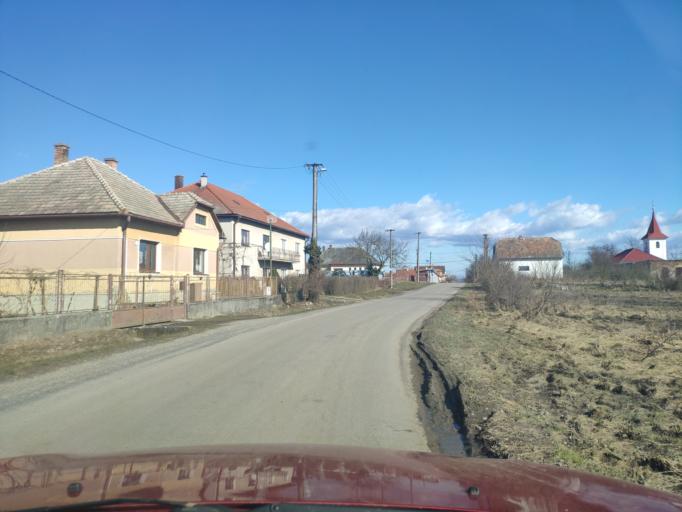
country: HU
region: Borsod-Abauj-Zemplen
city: Arlo
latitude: 48.2981
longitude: 20.1696
